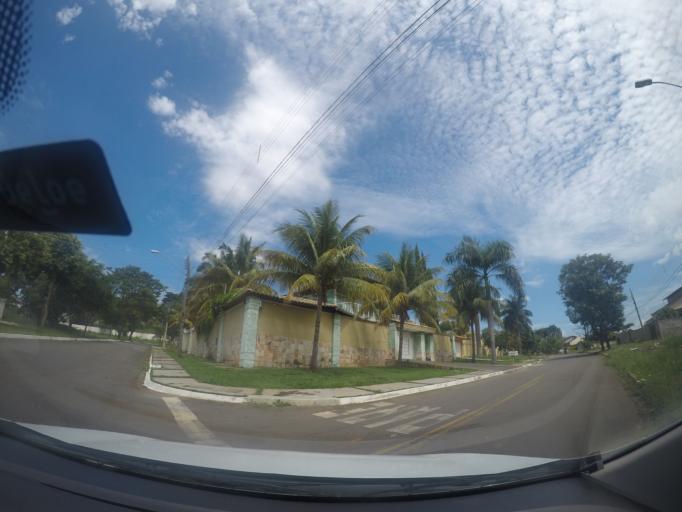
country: BR
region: Goias
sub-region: Goiania
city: Goiania
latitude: -16.6620
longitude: -49.3363
